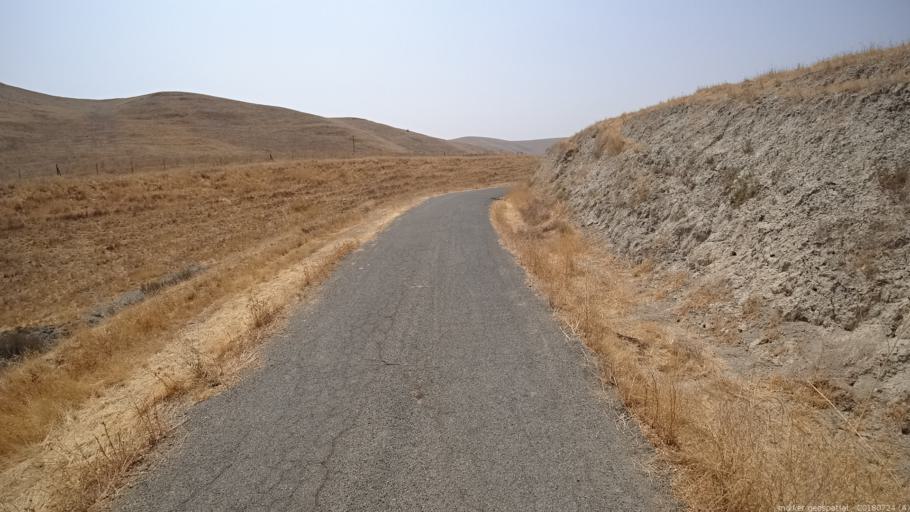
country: US
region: California
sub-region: Monterey County
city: King City
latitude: 36.1964
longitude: -120.9513
